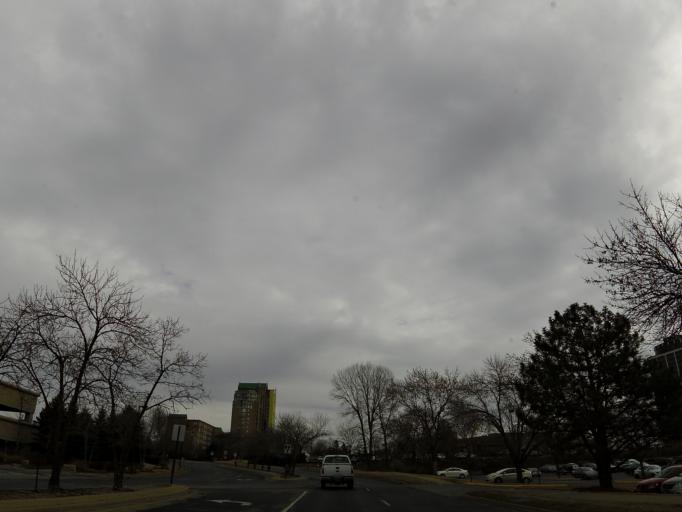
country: US
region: Minnesota
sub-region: Hennepin County
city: Bloomington
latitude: 44.8619
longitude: -93.3266
